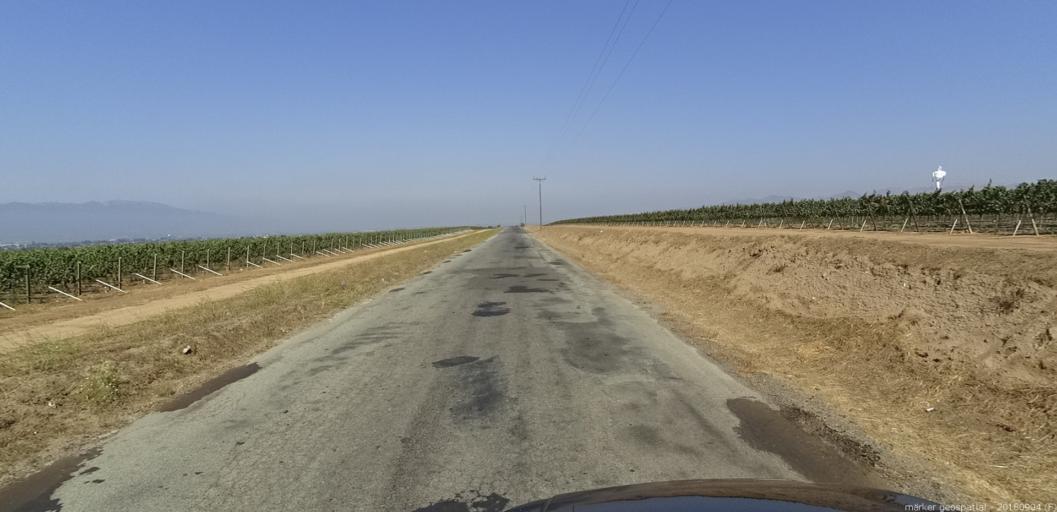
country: US
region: California
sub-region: Monterey County
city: Gonzales
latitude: 36.5075
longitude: -121.4023
